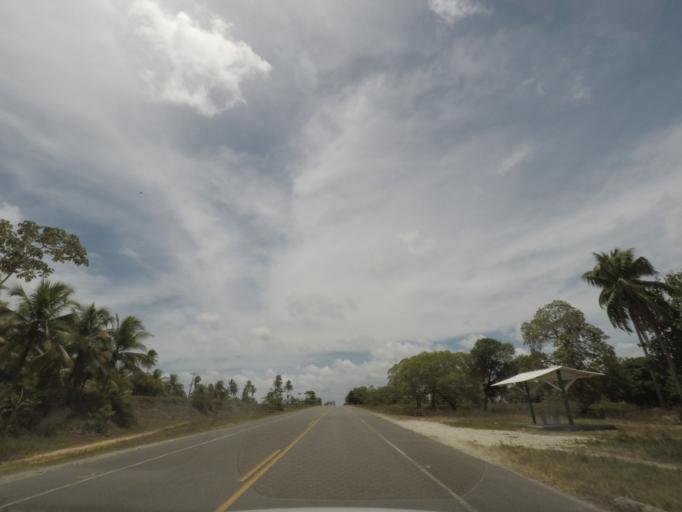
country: BR
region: Bahia
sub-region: Conde
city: Conde
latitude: -11.7828
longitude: -37.6158
